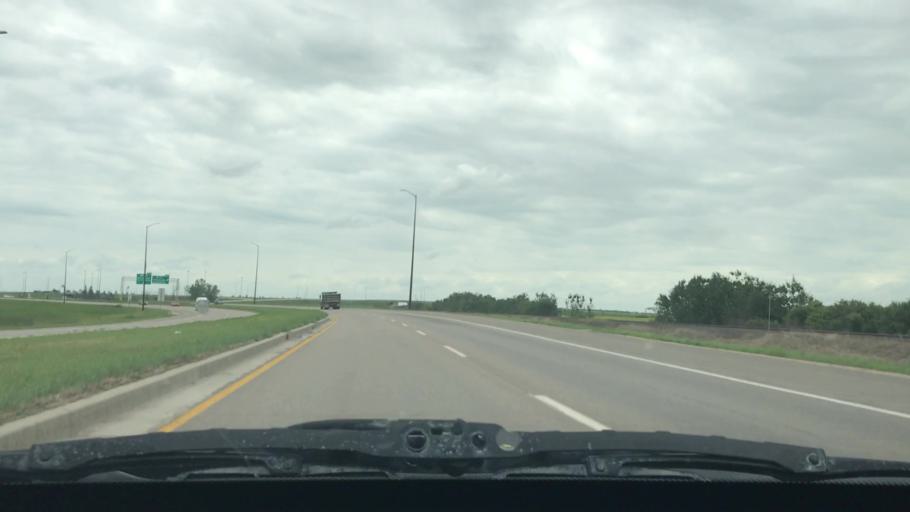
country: CA
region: Manitoba
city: Winnipeg
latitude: 49.8370
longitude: -96.9766
